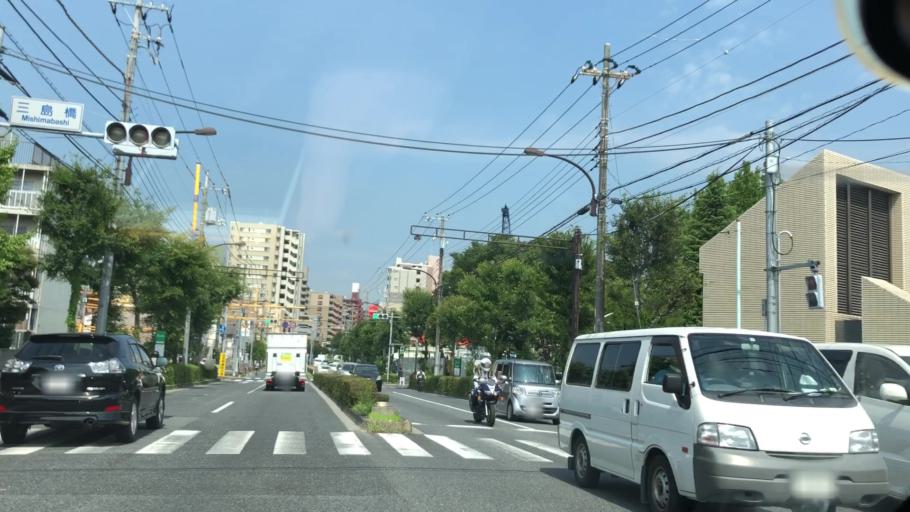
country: JP
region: Tokyo
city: Urayasu
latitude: 35.6842
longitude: 139.8720
